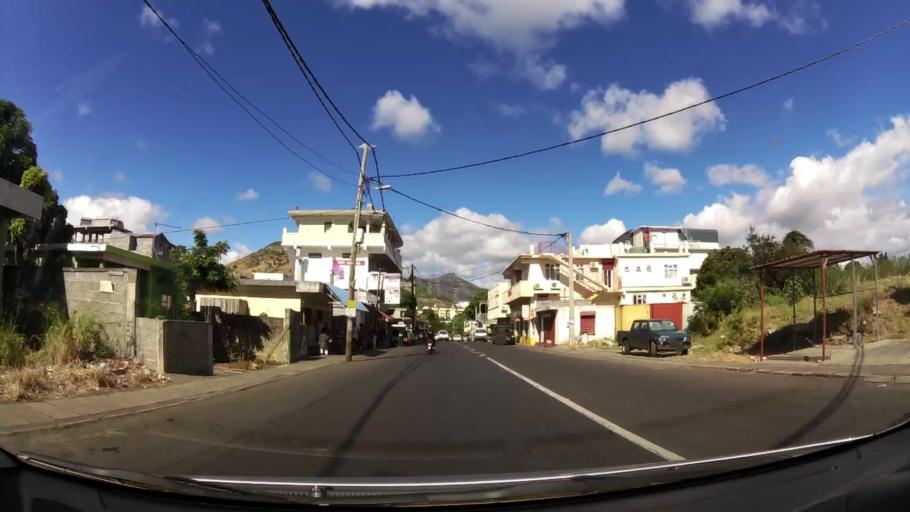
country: MU
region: Pamplemousses
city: Le Hochet
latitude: -20.1496
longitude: 57.5227
